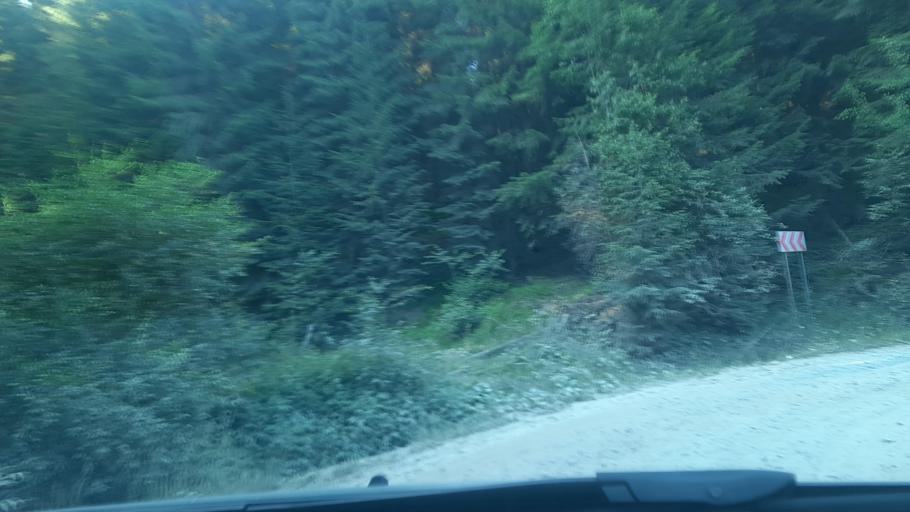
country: RO
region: Alba
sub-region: Comuna Sugag
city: Sugag
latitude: 45.5821
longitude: 23.6089
